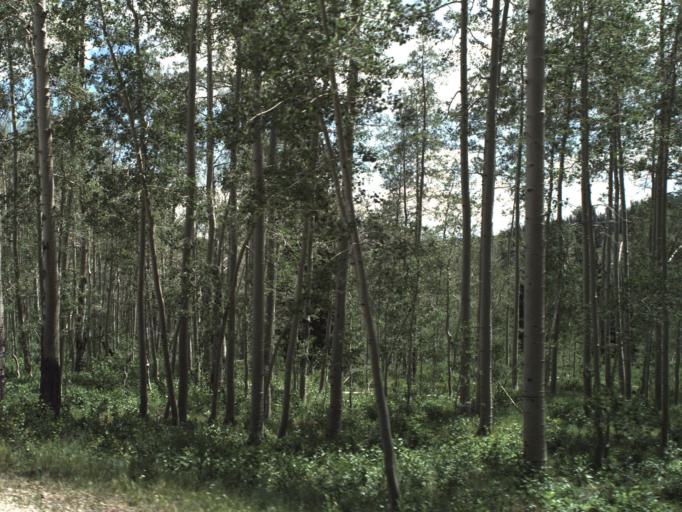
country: US
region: Utah
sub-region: Rich County
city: Randolph
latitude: 41.4746
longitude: -111.4872
